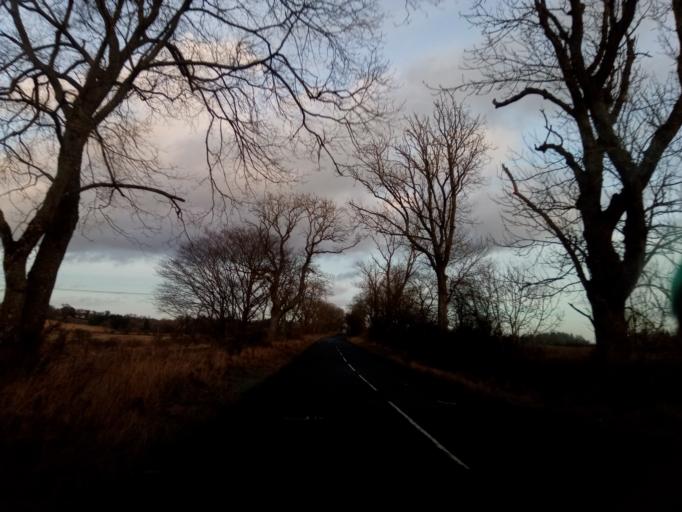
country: GB
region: Scotland
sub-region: The Scottish Borders
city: Melrose
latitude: 55.5575
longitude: -2.7196
